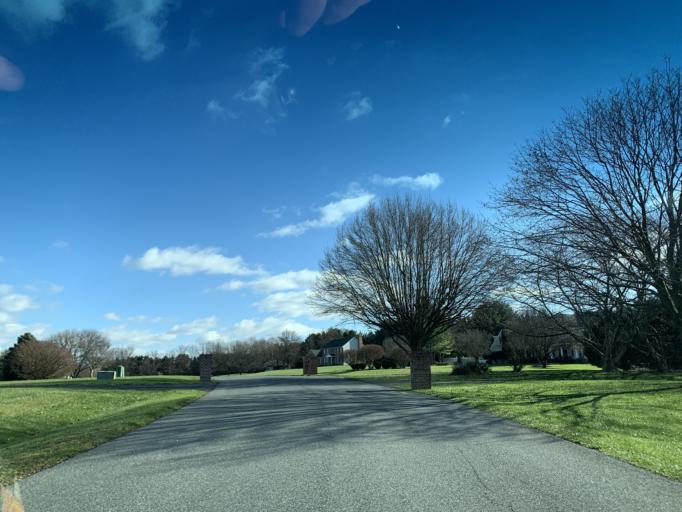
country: US
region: Maryland
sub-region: Harford County
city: South Bel Air
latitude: 39.5679
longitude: -76.2577
